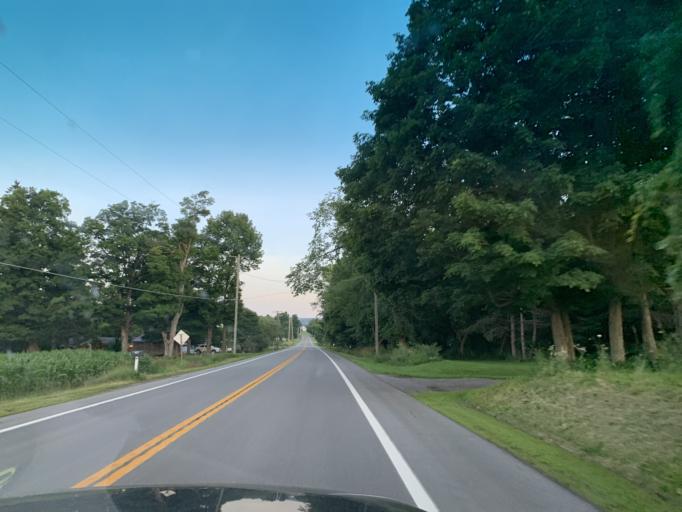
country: US
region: New York
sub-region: Oneida County
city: Chadwicks
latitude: 42.9281
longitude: -75.2485
